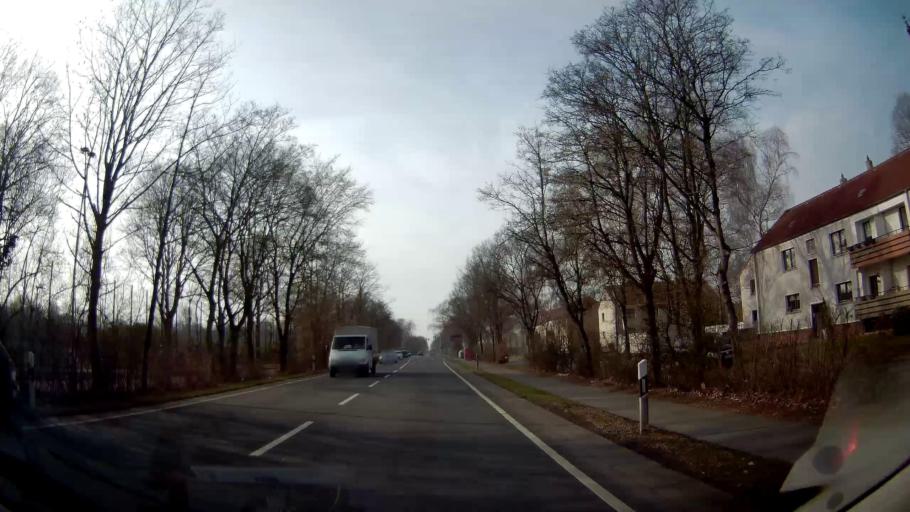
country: DE
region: North Rhine-Westphalia
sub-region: Regierungsbezirk Munster
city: Bottrop
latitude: 51.5296
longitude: 6.8722
